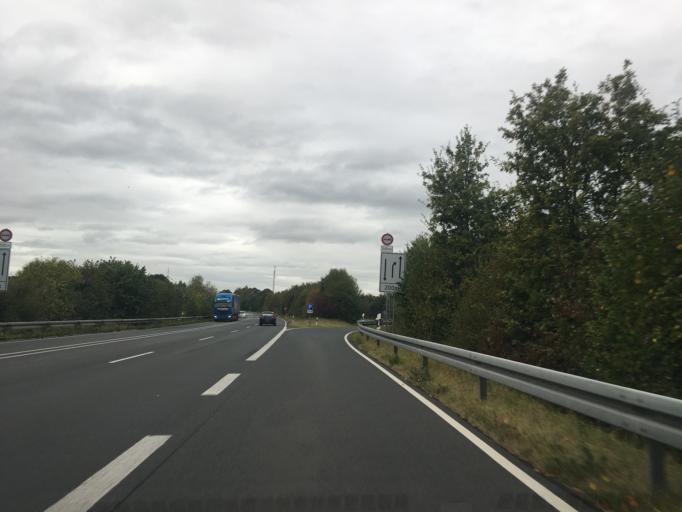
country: DE
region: North Rhine-Westphalia
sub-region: Regierungsbezirk Munster
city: Ochtrup
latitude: 52.1937
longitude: 7.1957
